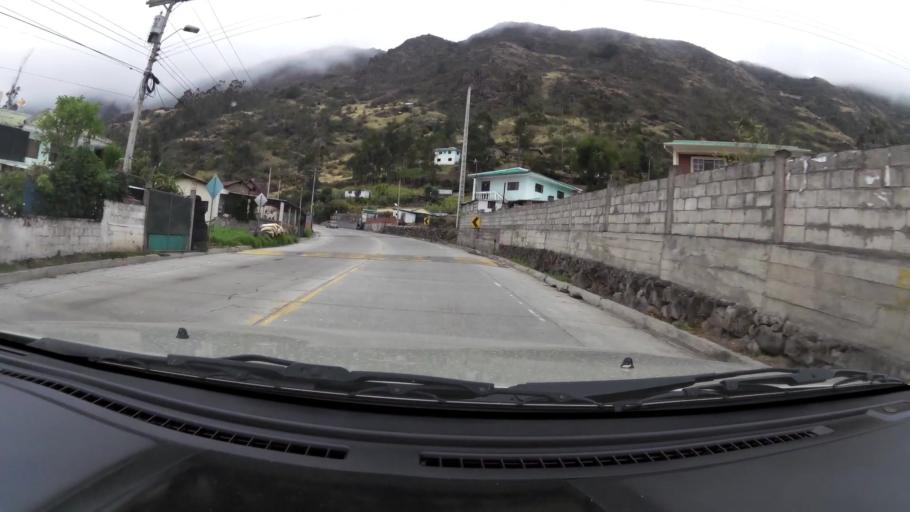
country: EC
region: Canar
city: Canar
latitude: -2.4811
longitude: -78.9850
